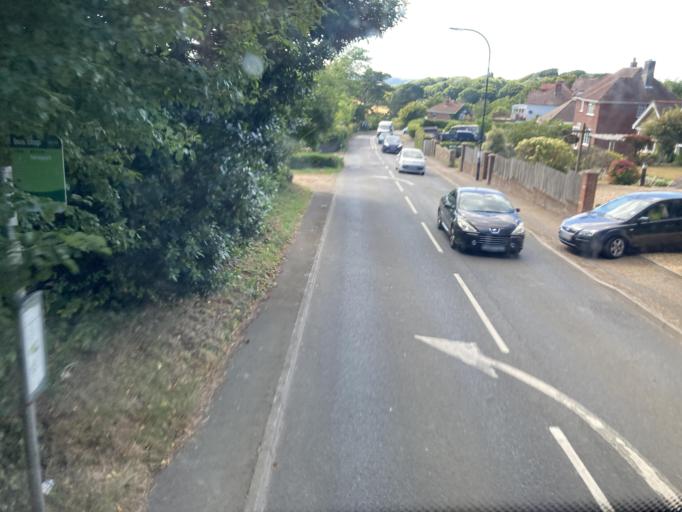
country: GB
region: England
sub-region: Isle of Wight
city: Shanklin
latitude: 50.6277
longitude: -1.1955
